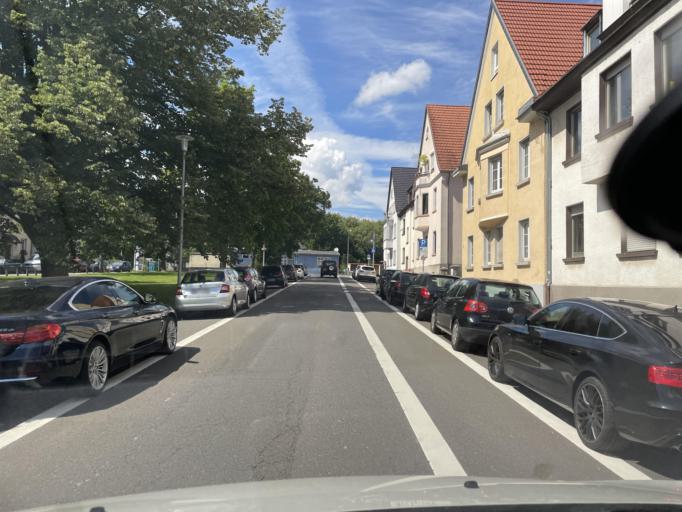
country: DE
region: Saarland
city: Saarbrucken
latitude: 49.2418
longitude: 7.0160
